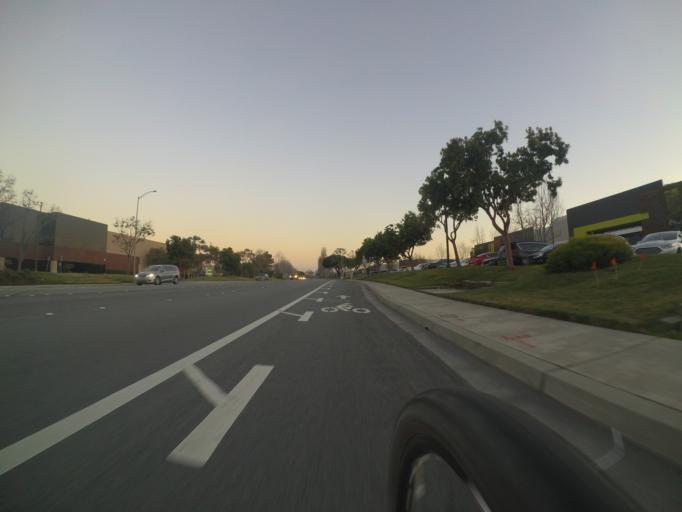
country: US
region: California
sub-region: Santa Clara County
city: Milpitas
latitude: 37.4733
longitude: -121.9417
